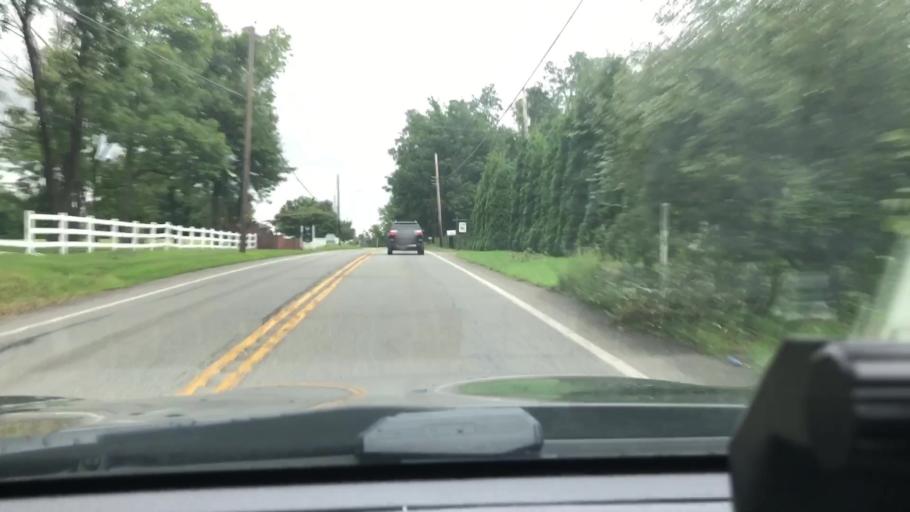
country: US
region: Pennsylvania
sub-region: Montgomery County
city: Gilbertsville
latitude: 40.3323
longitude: -75.5533
